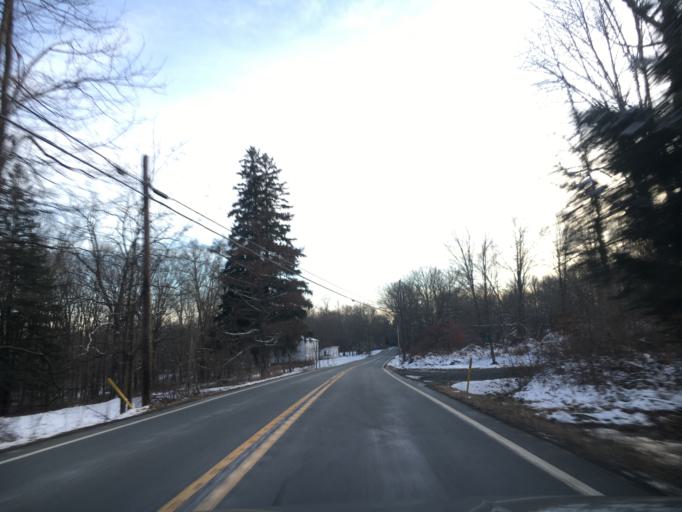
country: US
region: Pennsylvania
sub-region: Pike County
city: Saw Creek
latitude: 41.1827
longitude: -75.0818
